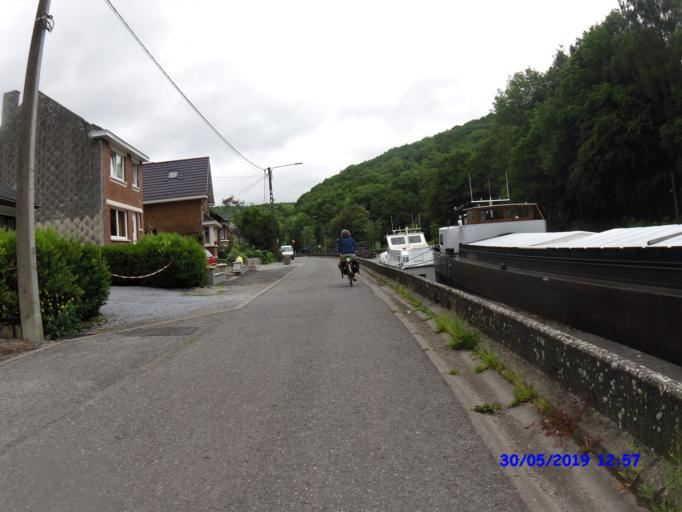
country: BE
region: Wallonia
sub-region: Province du Hainaut
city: Thuin
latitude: 50.3428
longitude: 4.2925
